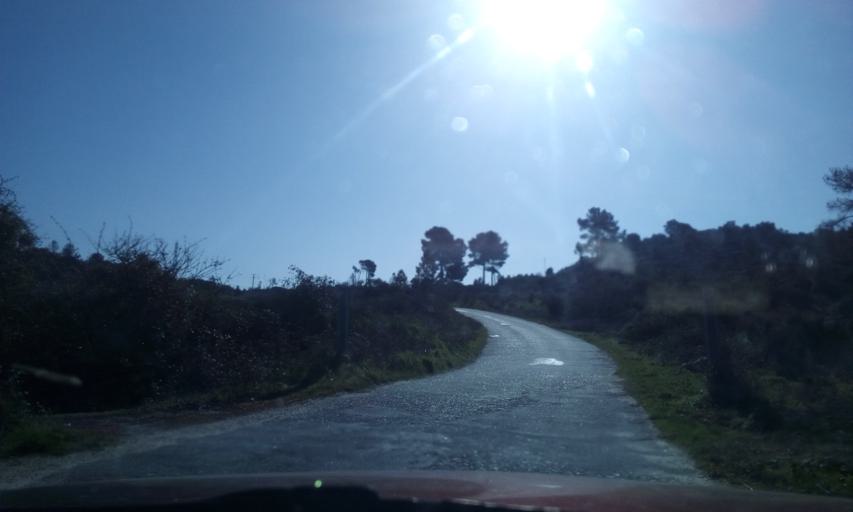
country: PT
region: Guarda
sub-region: Celorico da Beira
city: Celorico da Beira
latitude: 40.6908
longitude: -7.4216
